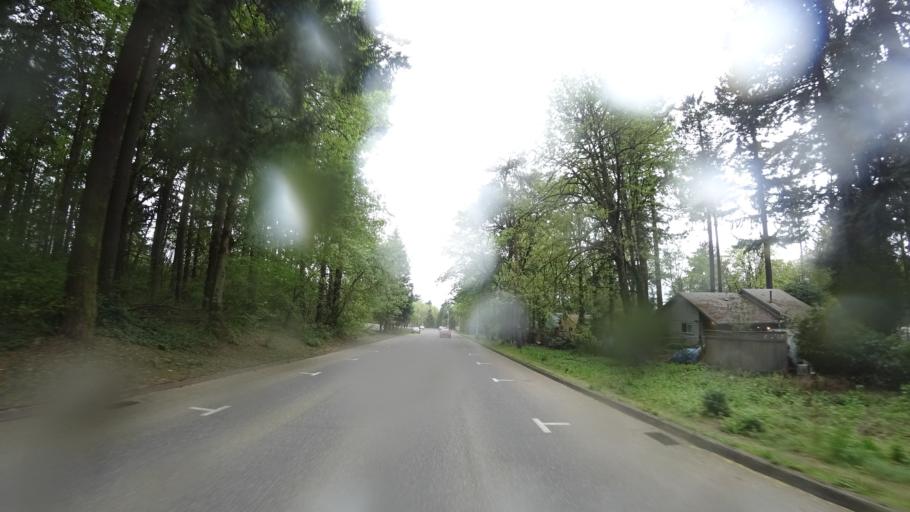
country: US
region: Oregon
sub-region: Washington County
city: Metzger
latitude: 45.4413
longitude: -122.7320
